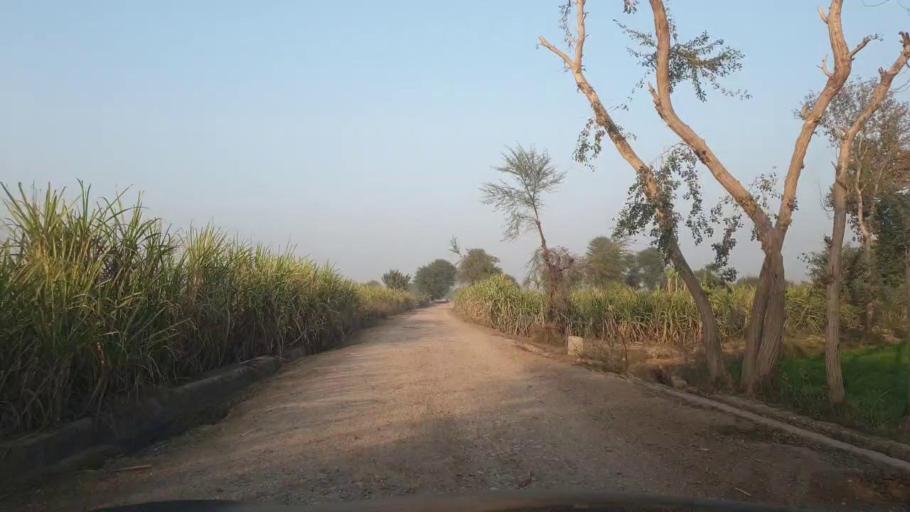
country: PK
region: Sindh
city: Ubauro
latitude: 28.3263
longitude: 69.7766
